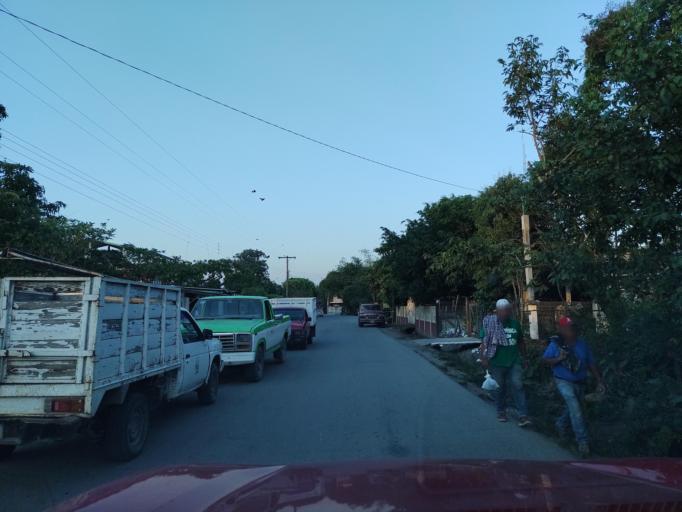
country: MX
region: Veracruz
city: Agua Dulce
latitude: 20.3180
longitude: -97.2709
